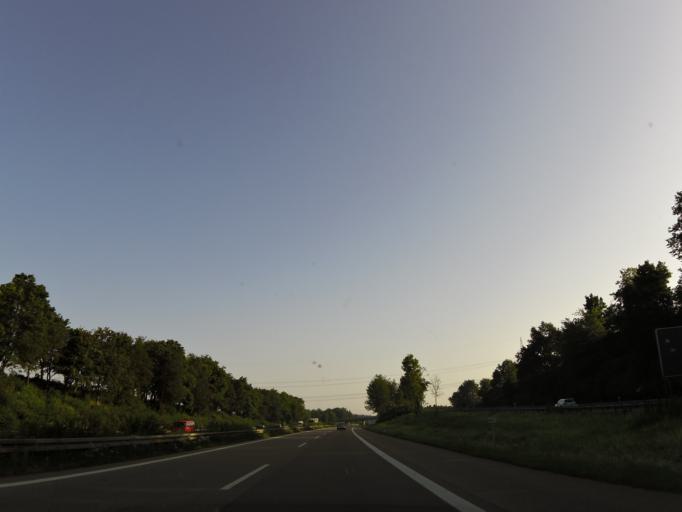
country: DE
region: Bavaria
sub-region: Swabia
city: Vohringen
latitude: 48.3205
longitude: 10.0901
